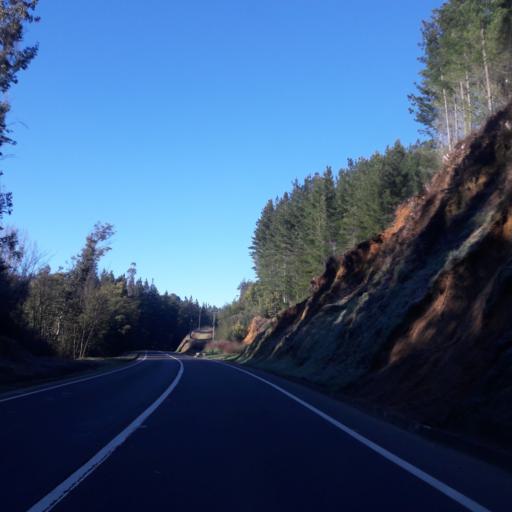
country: CL
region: Biobio
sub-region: Provincia de Concepcion
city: Lota
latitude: -37.2457
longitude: -72.9632
